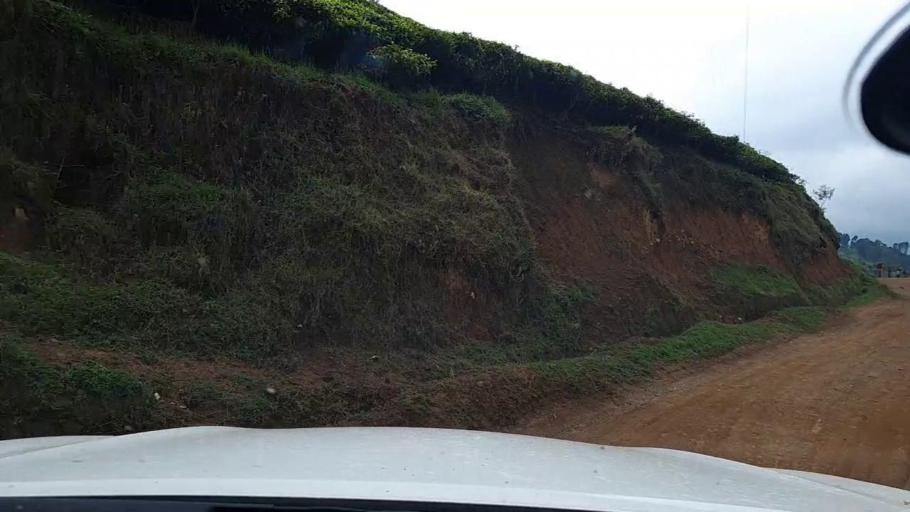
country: RW
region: Western Province
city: Kibuye
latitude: -2.1689
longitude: 29.4259
